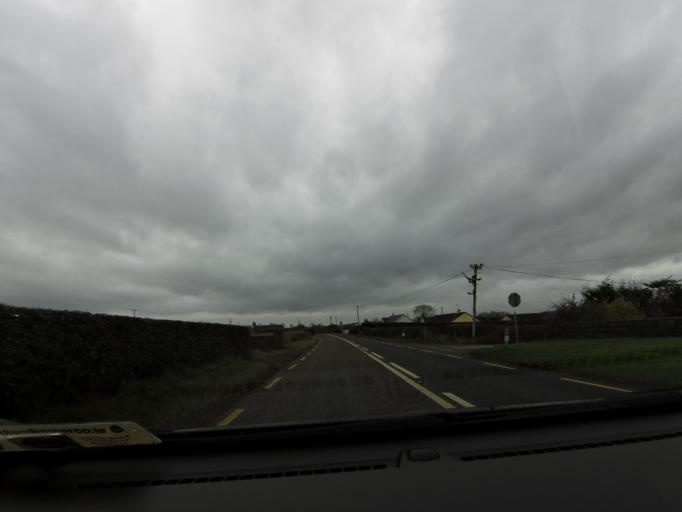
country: IE
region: Leinster
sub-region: Kilkenny
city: Ballyragget
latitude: 52.7602
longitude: -7.3305
